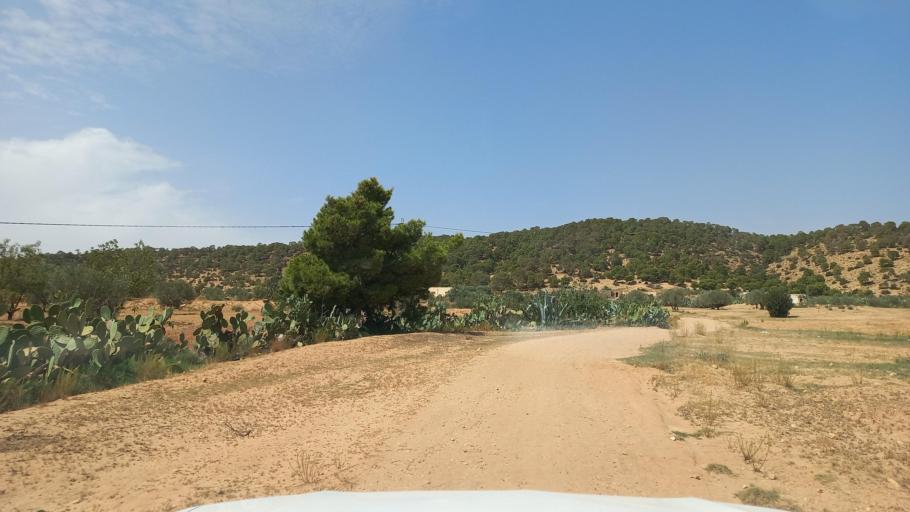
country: TN
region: Al Qasrayn
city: Kasserine
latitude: 35.3772
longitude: 8.9103
